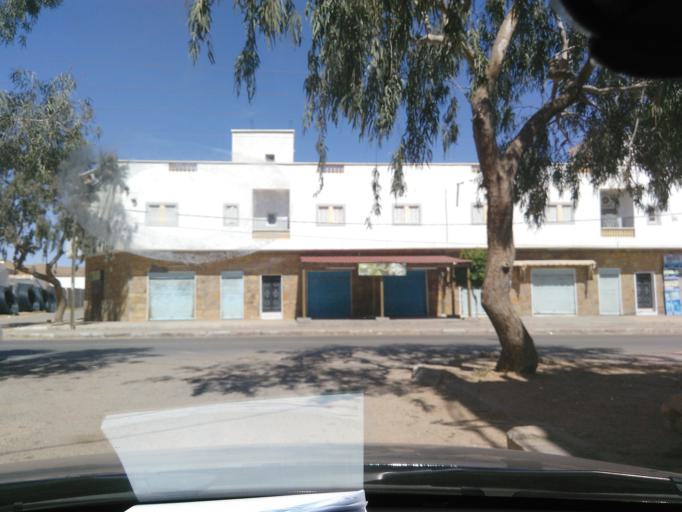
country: TN
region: Tataouine
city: Tataouine
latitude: 32.9516
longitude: 10.4670
